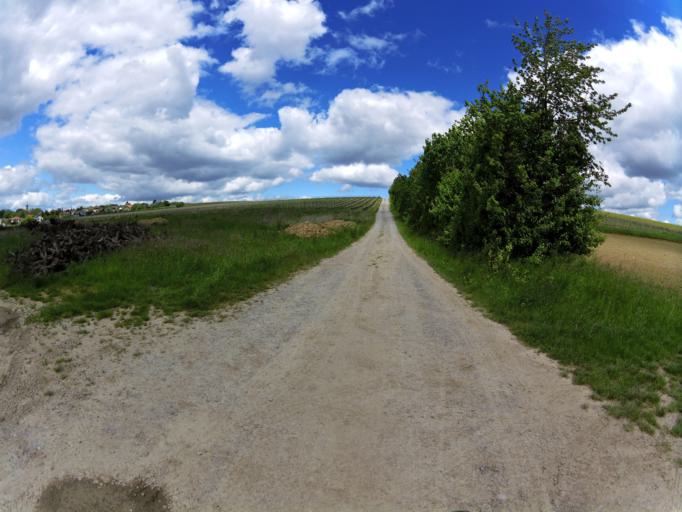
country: DE
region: Bavaria
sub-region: Regierungsbezirk Unterfranken
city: Volkach
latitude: 49.8873
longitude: 10.2367
